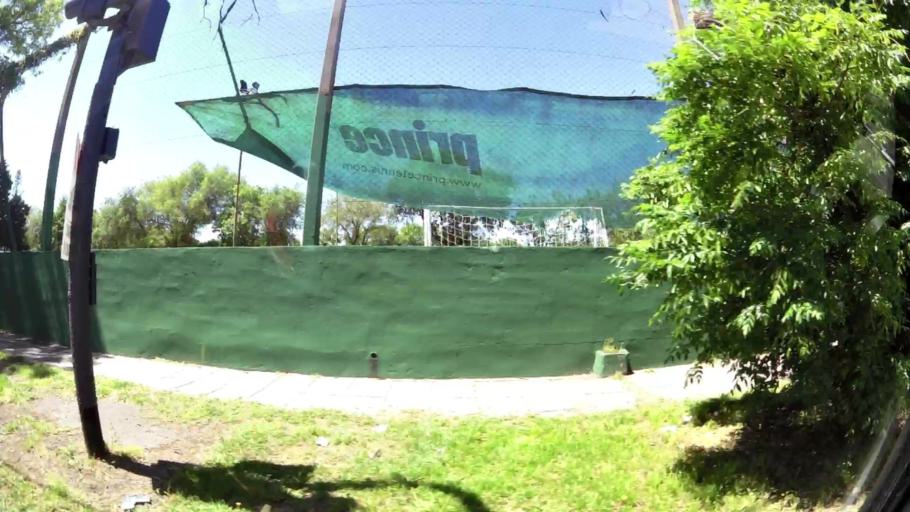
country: AR
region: Buenos Aires
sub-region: Partido de Vicente Lopez
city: Olivos
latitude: -34.5143
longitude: -58.5054
